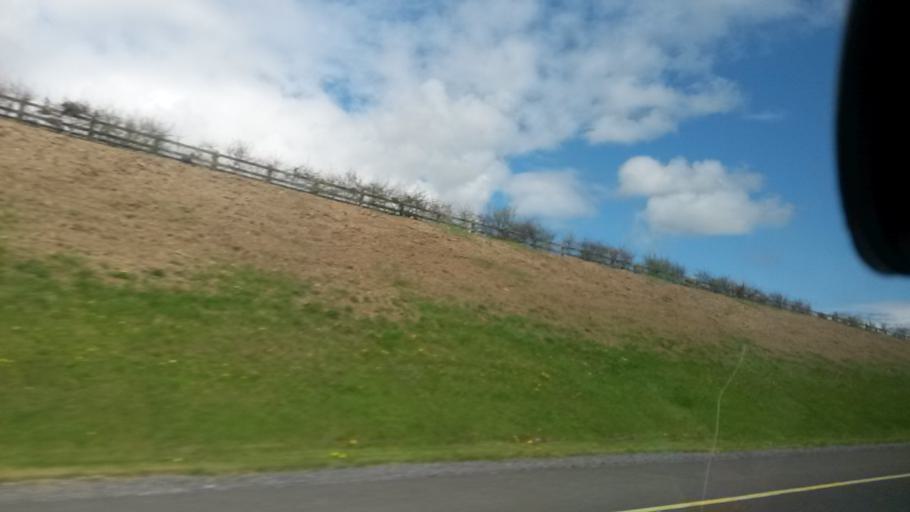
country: IE
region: Leinster
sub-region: Kildare
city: Kildare
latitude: 53.1567
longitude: -6.8653
